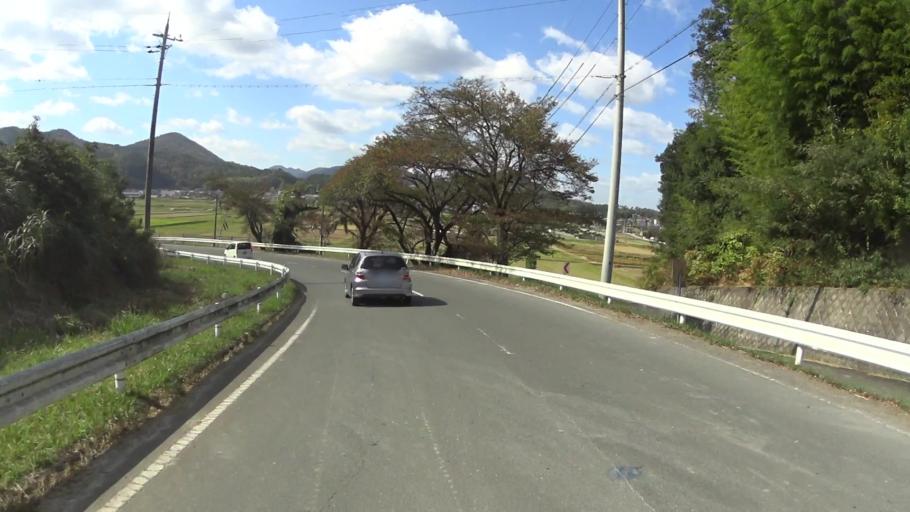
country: JP
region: Kyoto
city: Kameoka
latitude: 35.1606
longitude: 135.4354
